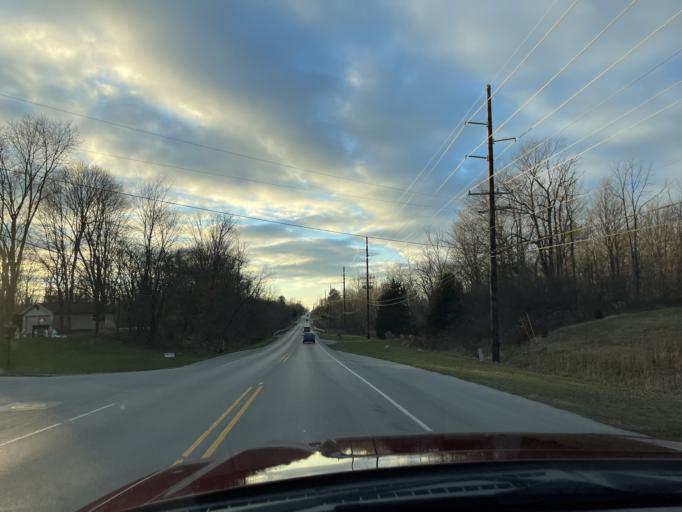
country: US
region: Indiana
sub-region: Hendricks County
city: Avon
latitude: 39.7622
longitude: -86.4423
